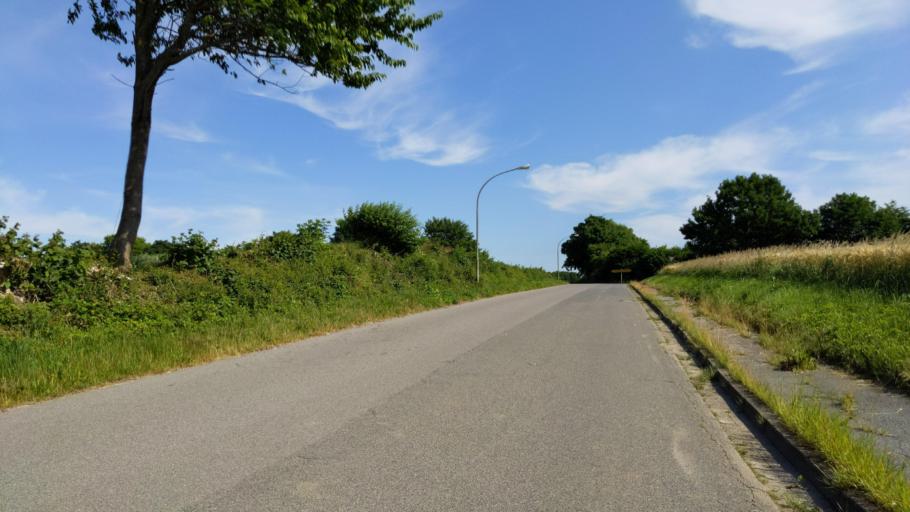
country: DE
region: Schleswig-Holstein
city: Scharbeutz
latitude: 54.0170
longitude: 10.7109
